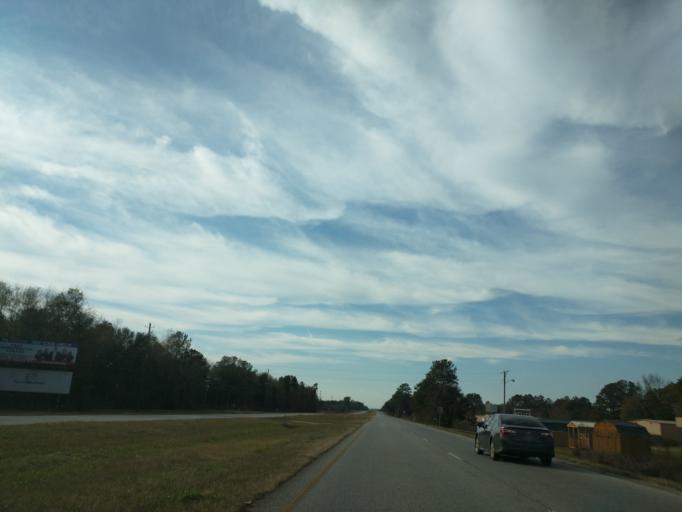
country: US
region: Georgia
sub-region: Decatur County
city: Bainbridge
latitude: 30.8913
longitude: -84.4907
